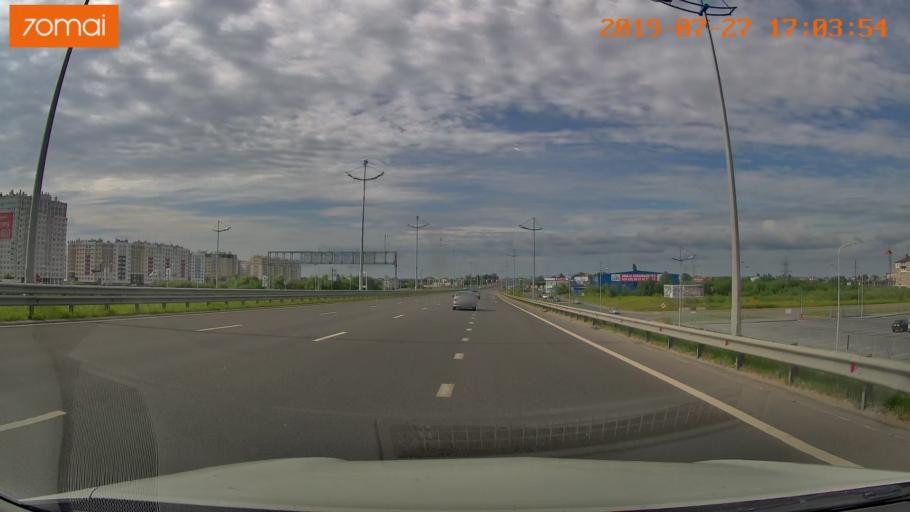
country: RU
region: Kaliningrad
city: Bol'shoe Isakovo
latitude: 54.7085
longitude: 20.5982
